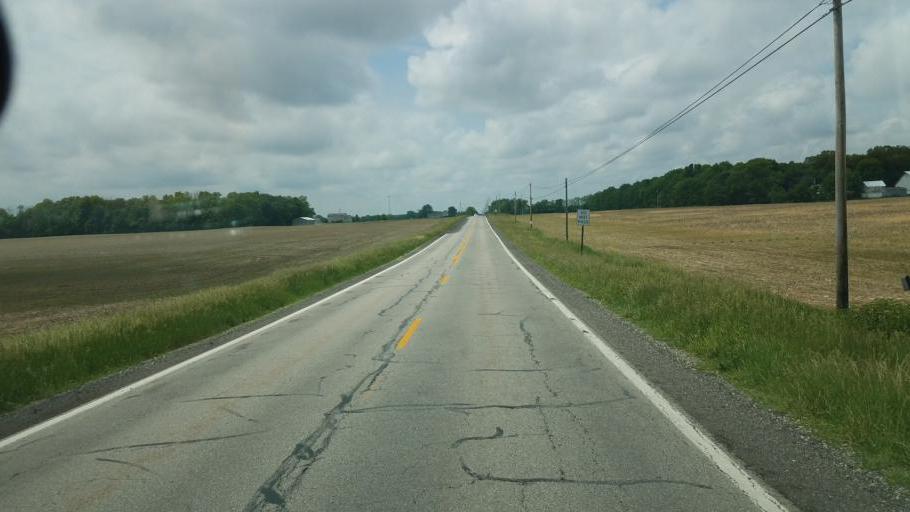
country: US
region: Ohio
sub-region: Marion County
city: Prospect
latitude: 40.4500
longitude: -83.1976
